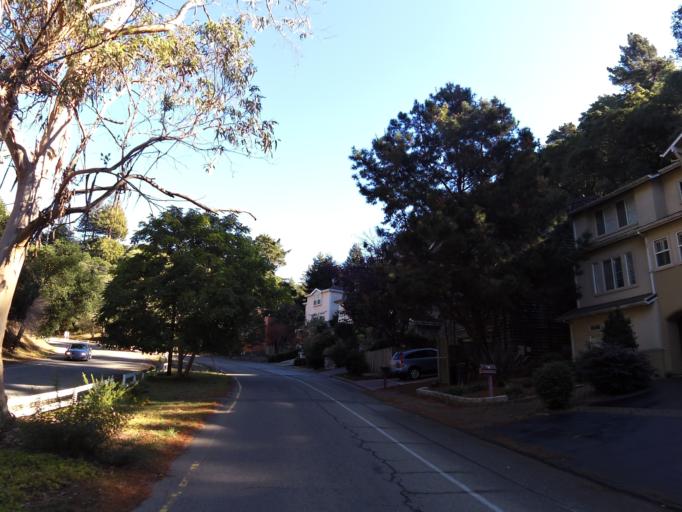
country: US
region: California
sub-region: Alameda County
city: Piedmont
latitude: 37.8304
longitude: -122.2238
